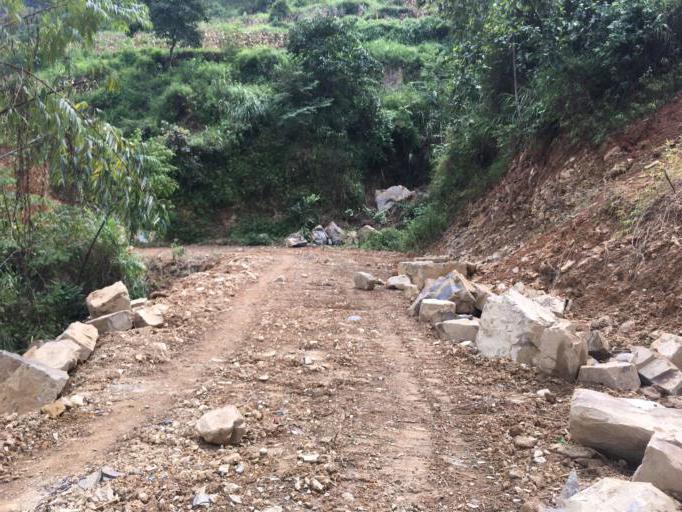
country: CN
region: Guangxi Zhuangzu Zizhiqu
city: Tongle
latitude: 25.3009
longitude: 106.1459
